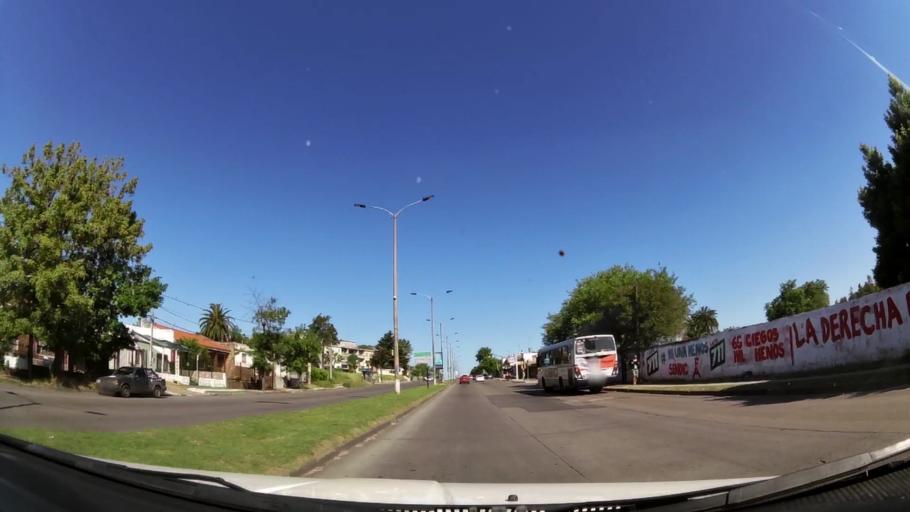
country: UY
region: Montevideo
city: Montevideo
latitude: -34.8406
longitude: -56.1979
